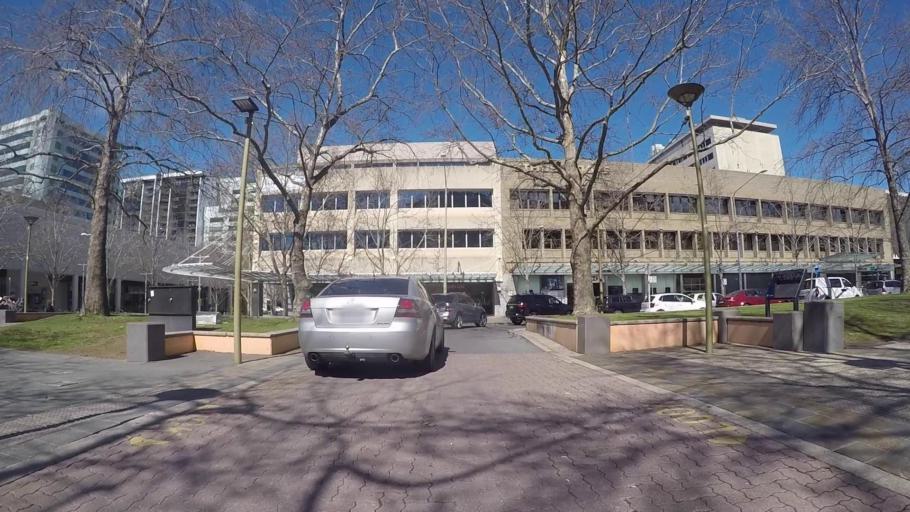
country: AU
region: Australian Capital Territory
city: Canberra
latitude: -35.2805
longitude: 149.1322
